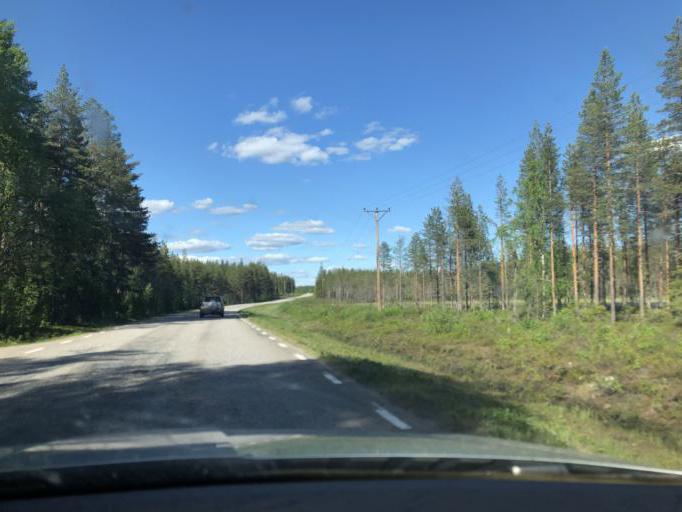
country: SE
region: Norrbotten
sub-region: Kalix Kommun
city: Kalix
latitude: 66.0460
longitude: 23.1800
